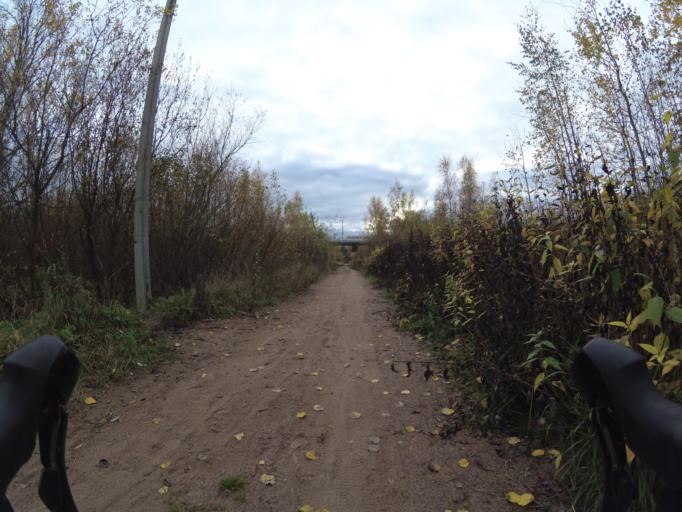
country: RU
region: St.-Petersburg
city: Lakhtinskiy
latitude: 60.0057
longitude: 30.1441
